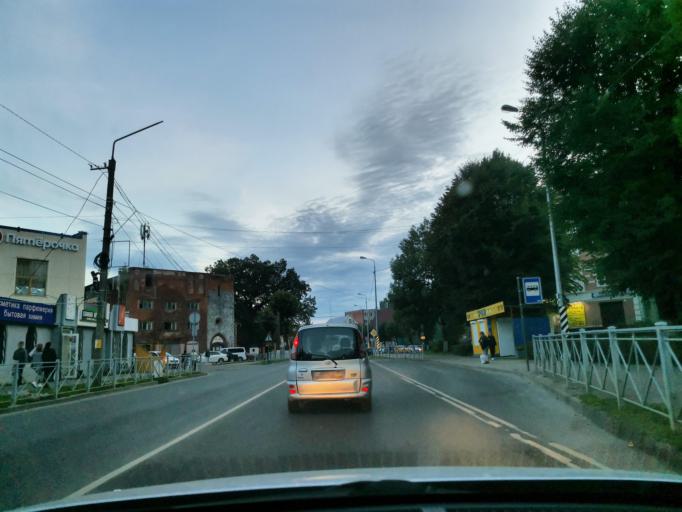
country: RU
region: Kaliningrad
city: Sovetsk
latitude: 55.0790
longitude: 21.8866
